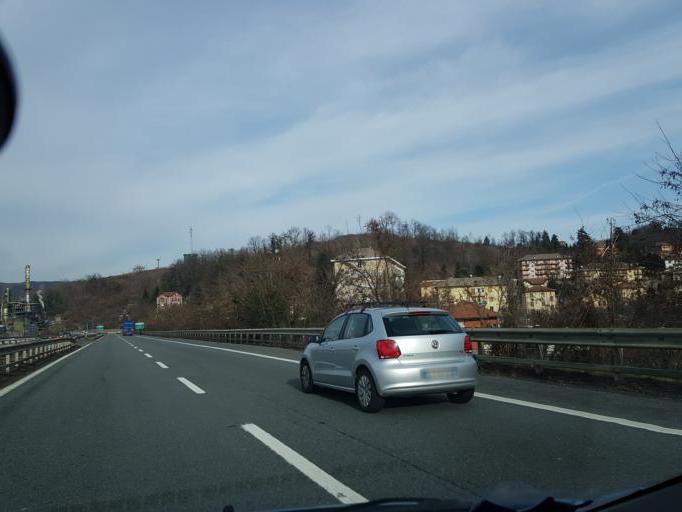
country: IT
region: Liguria
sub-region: Provincia di Genova
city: Busalla
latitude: 44.5726
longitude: 8.9507
